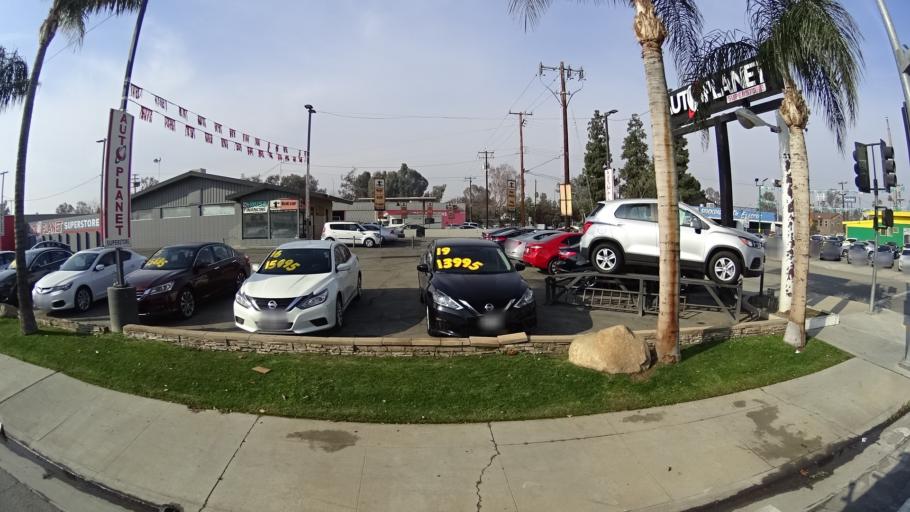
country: US
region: California
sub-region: Kern County
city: Bakersfield
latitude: 35.3647
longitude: -119.0389
